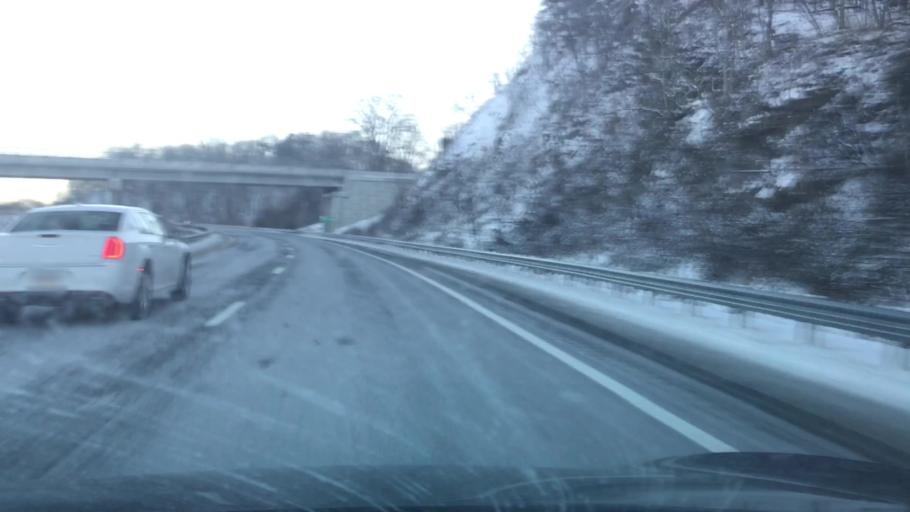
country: US
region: Virginia
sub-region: Montgomery County
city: Shawsville
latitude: 37.1952
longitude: -80.2700
